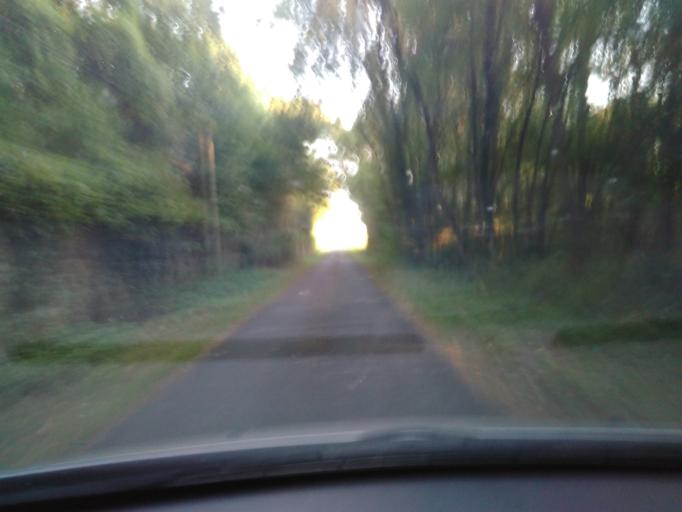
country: FR
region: Pays de la Loire
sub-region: Departement de Maine-et-Loire
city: Saint-Saturnin-sur-Loire
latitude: 47.3933
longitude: -0.4175
